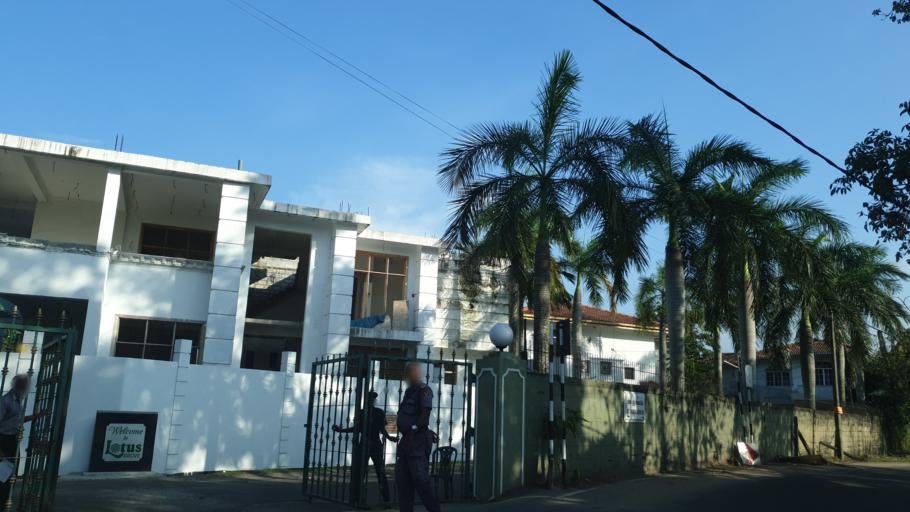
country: LK
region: Western
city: Galkissa
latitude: 6.8454
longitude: 79.8781
